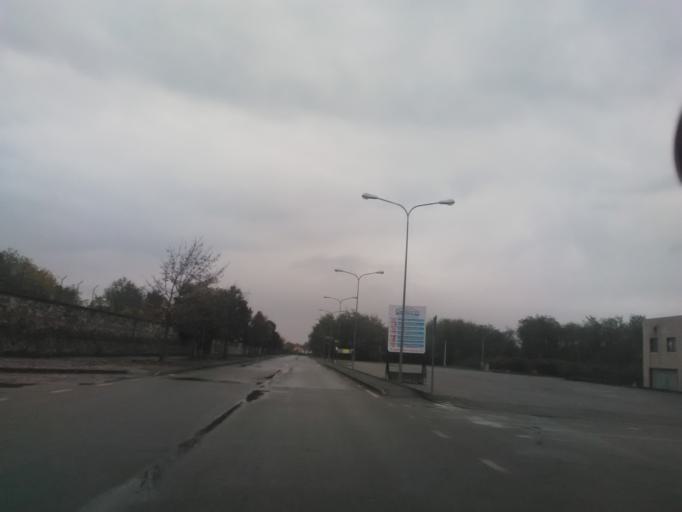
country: IT
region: Piedmont
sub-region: Provincia di Vercelli
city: Gattinara
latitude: 45.6075
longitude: 8.3648
